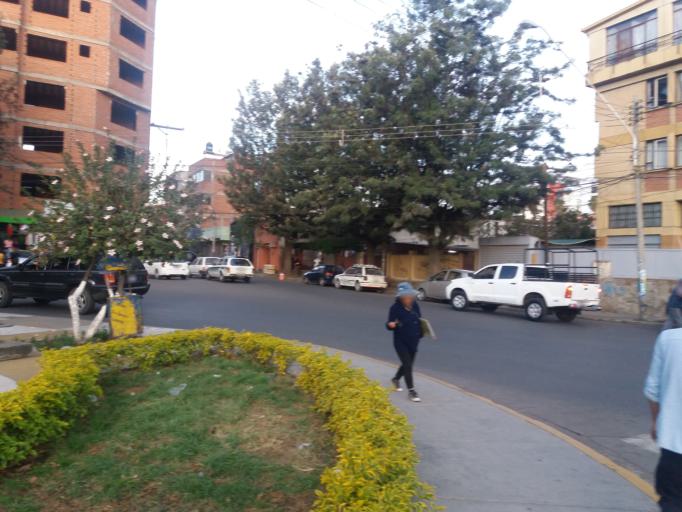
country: BO
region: Cochabamba
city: Cochabamba
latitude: -17.3896
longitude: -66.1502
